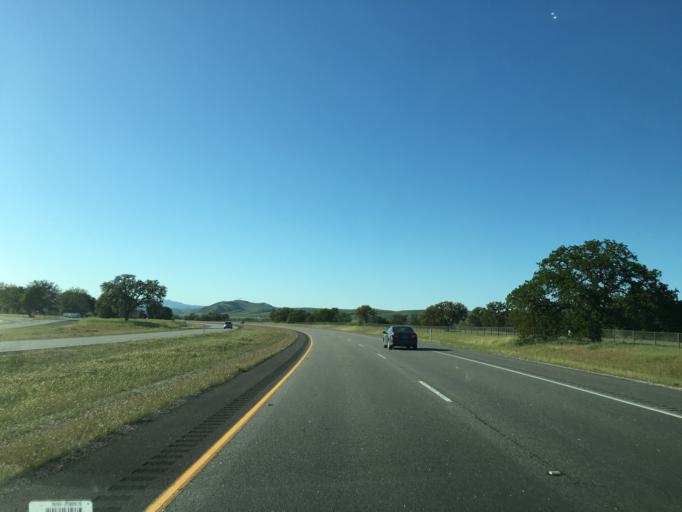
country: US
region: California
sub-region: San Luis Obispo County
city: San Miguel
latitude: 35.8490
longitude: -120.7656
